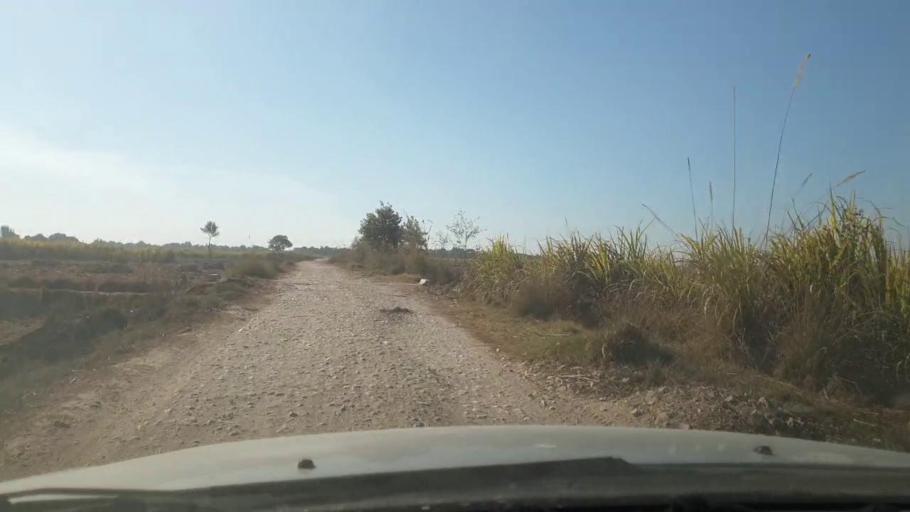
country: PK
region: Sindh
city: Ghotki
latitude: 27.9783
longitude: 69.1957
